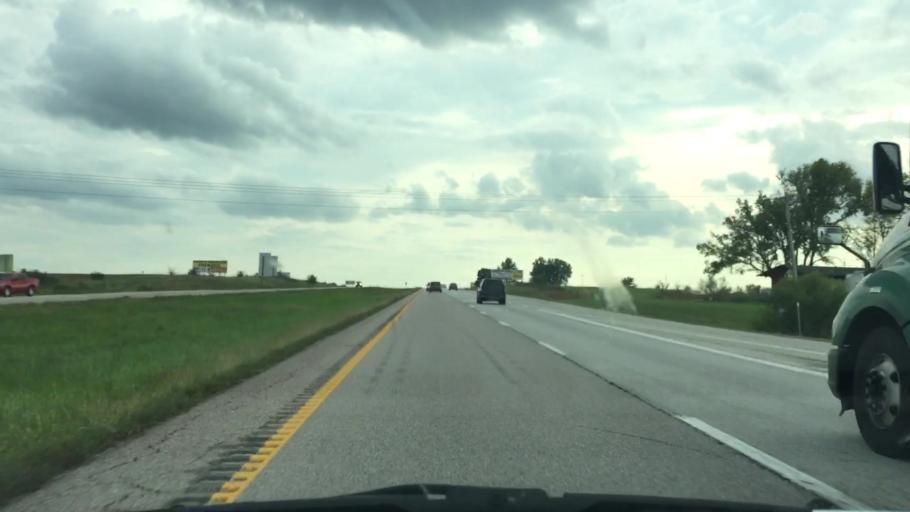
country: US
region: Missouri
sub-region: Clinton County
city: Lathrop
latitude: 39.5503
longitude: -94.2706
